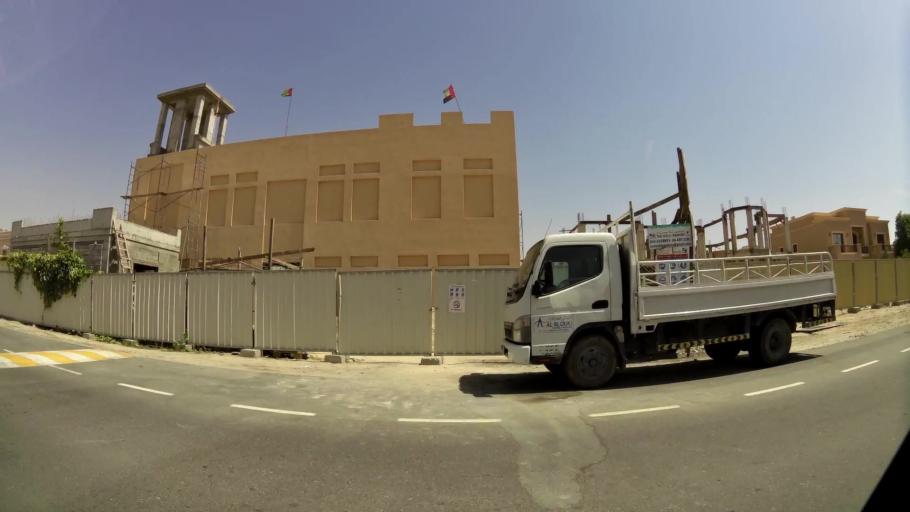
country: AE
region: Dubai
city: Dubai
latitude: 25.1015
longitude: 55.2095
